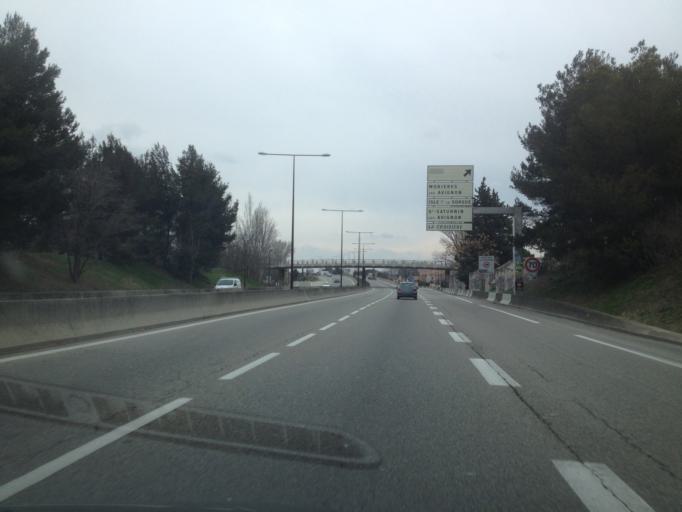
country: FR
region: Provence-Alpes-Cote d'Azur
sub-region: Departement du Vaucluse
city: Le Pontet
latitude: 43.9490
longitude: 4.8408
